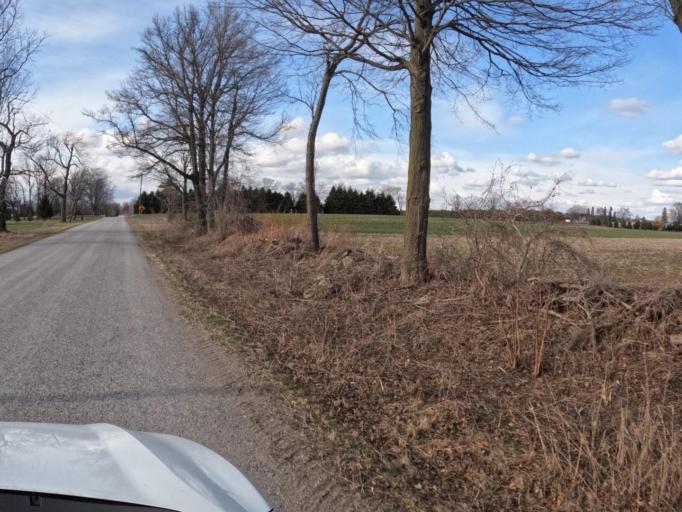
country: CA
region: Ontario
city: Brant
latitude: 43.0028
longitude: -80.4130
